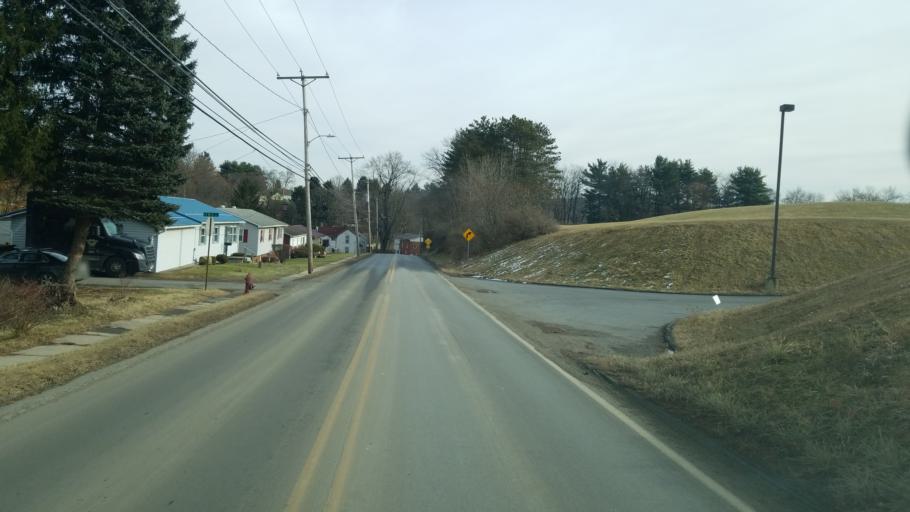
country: US
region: Pennsylvania
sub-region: Jefferson County
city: Punxsutawney
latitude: 40.9490
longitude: -78.9771
